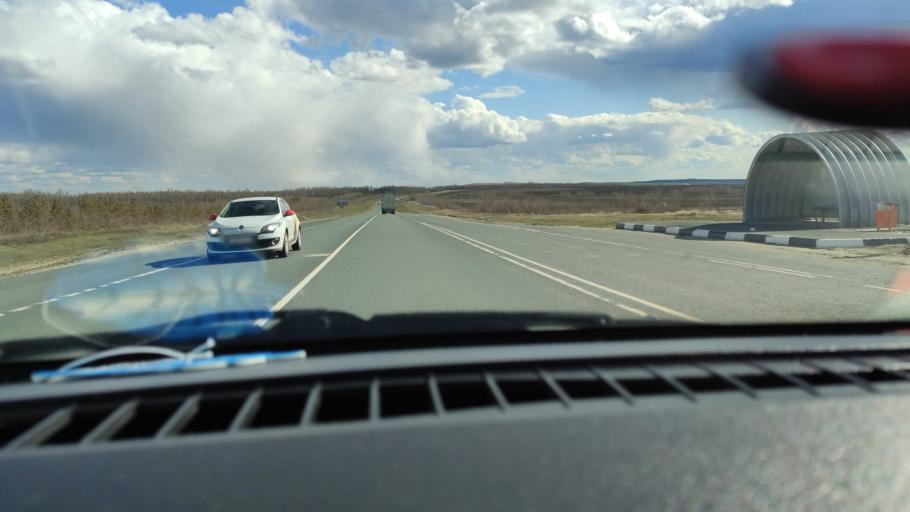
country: RU
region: Saratov
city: Alekseyevka
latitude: 52.2852
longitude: 47.9312
